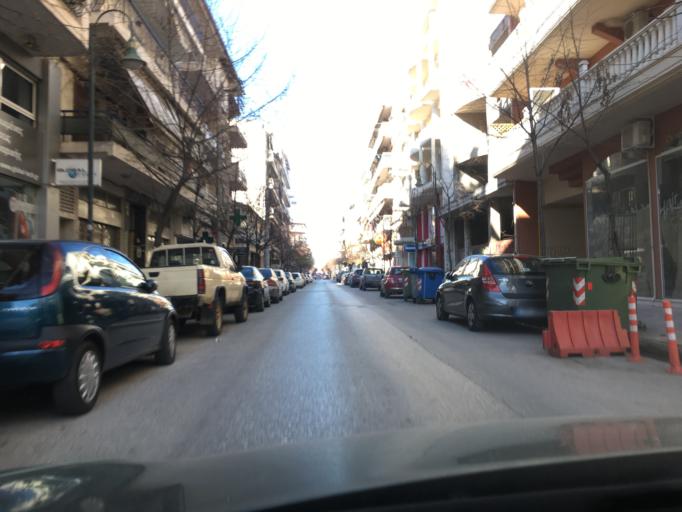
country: GR
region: Thessaly
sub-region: Nomos Larisis
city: Larisa
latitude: 39.6326
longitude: 22.4152
